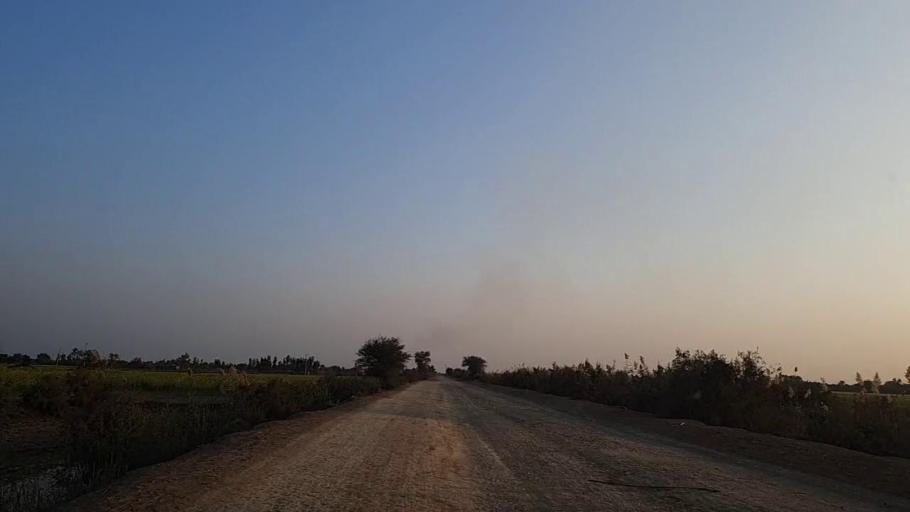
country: PK
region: Sindh
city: Shahdadpur
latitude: 25.9726
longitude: 68.4979
